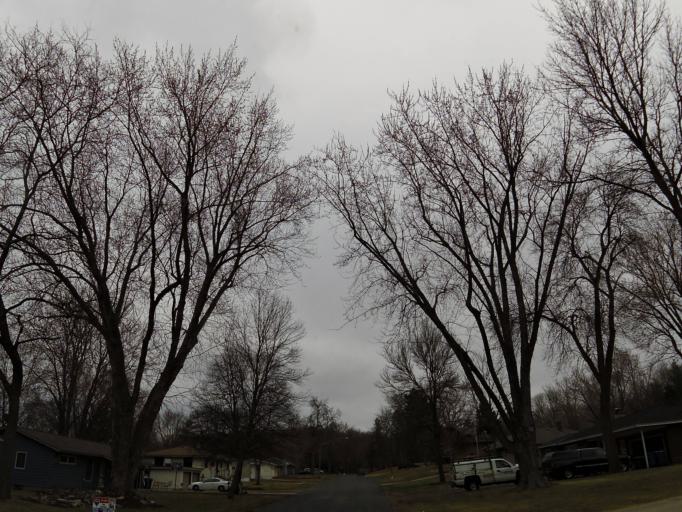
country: US
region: Minnesota
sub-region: Washington County
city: Bayport
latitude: 45.0205
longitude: -92.7882
